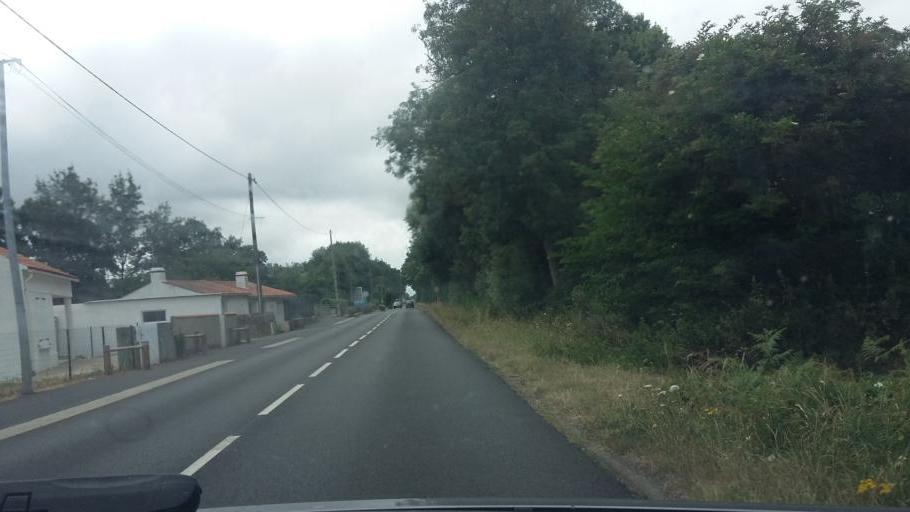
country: FR
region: Pays de la Loire
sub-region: Departement de la Vendee
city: Challans
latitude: 46.8395
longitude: -1.9005
